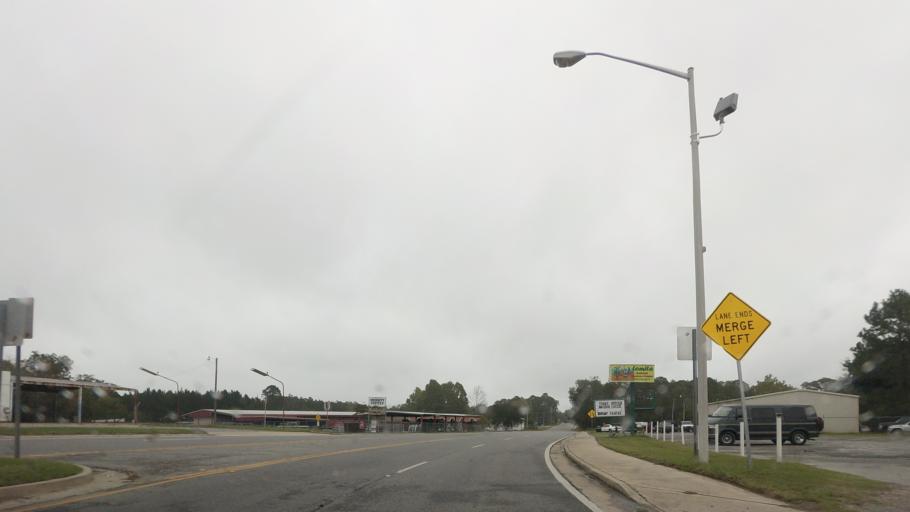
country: US
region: Georgia
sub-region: Ben Hill County
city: Fitzgerald
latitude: 31.7259
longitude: -83.2519
